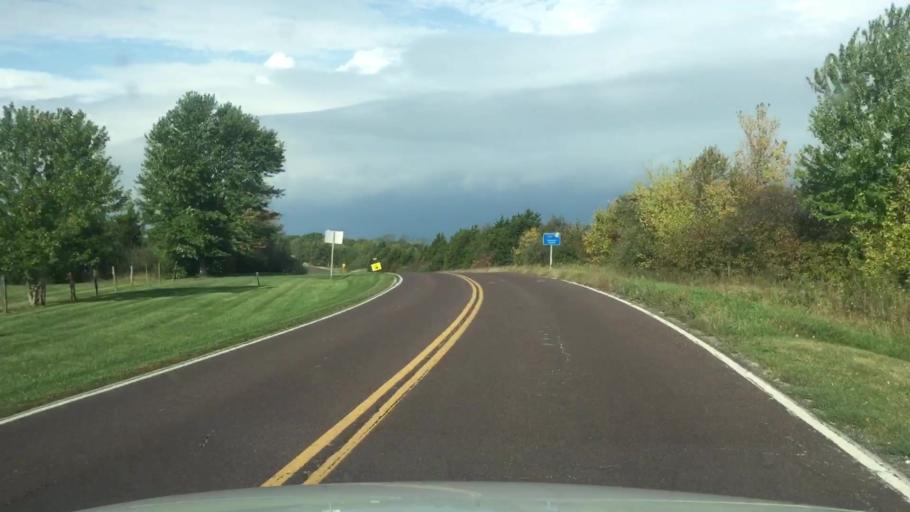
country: US
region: Missouri
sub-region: Boone County
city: Columbia
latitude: 38.8693
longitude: -92.2915
